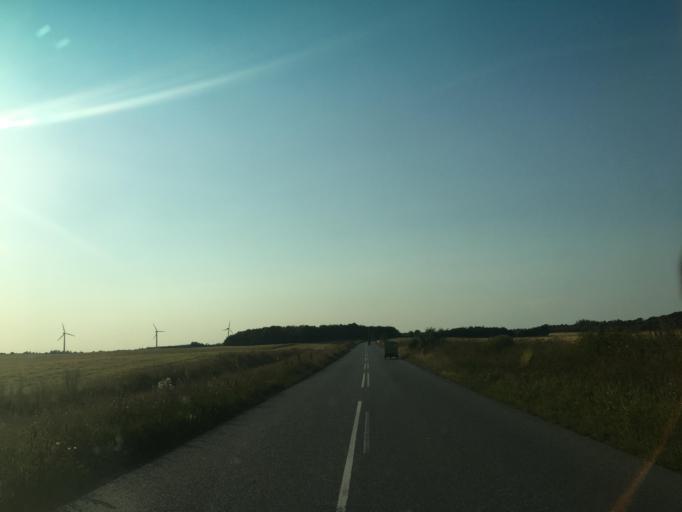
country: DK
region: North Denmark
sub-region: Thisted Kommune
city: Hurup
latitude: 56.7796
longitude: 8.4210
